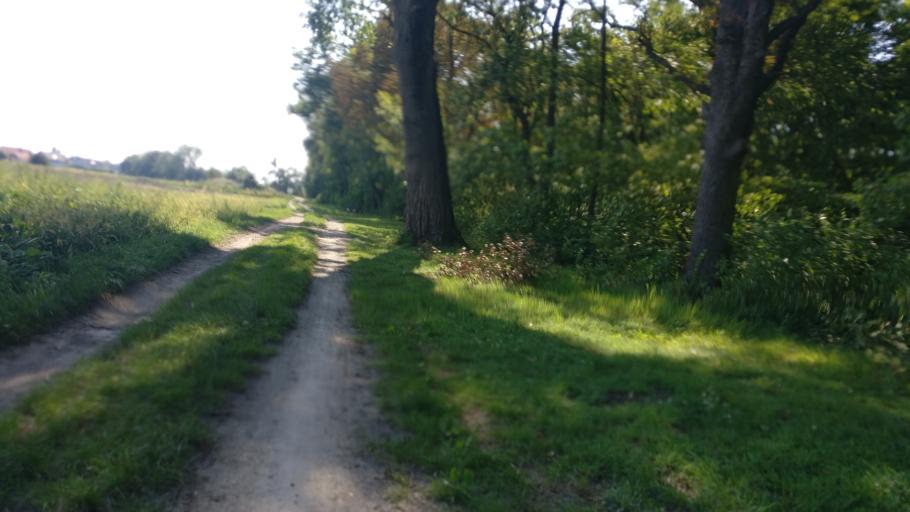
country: AT
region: Lower Austria
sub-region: Politischer Bezirk Baden
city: Mitterndorf an der Fischa
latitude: 47.9722
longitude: 16.4396
